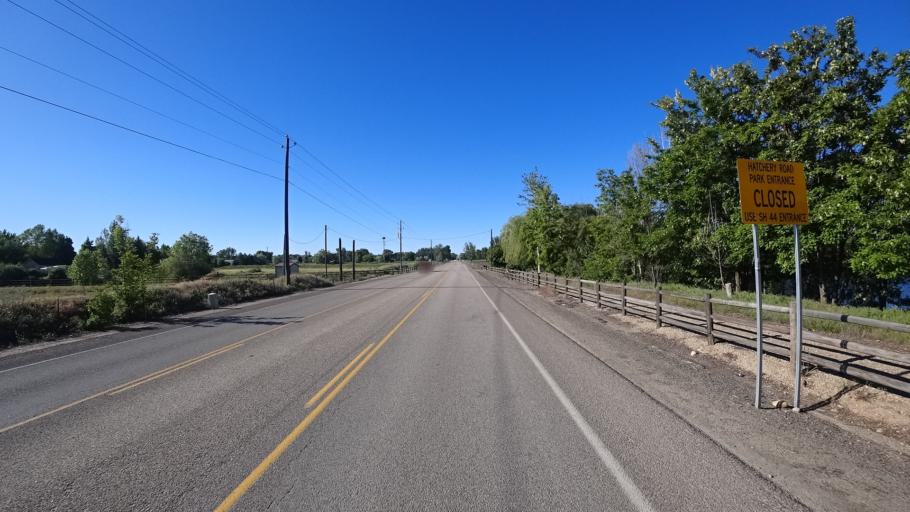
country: US
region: Idaho
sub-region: Ada County
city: Eagle
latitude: 43.6861
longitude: -116.4137
